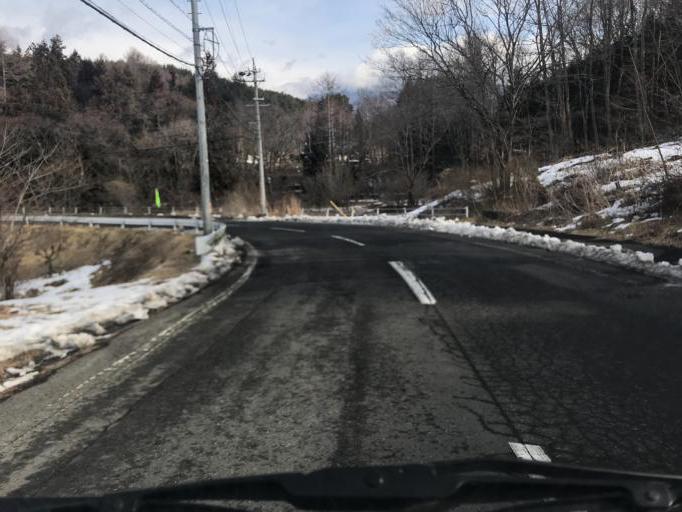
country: JP
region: Nagano
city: Chino
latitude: 35.8886
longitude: 138.2989
